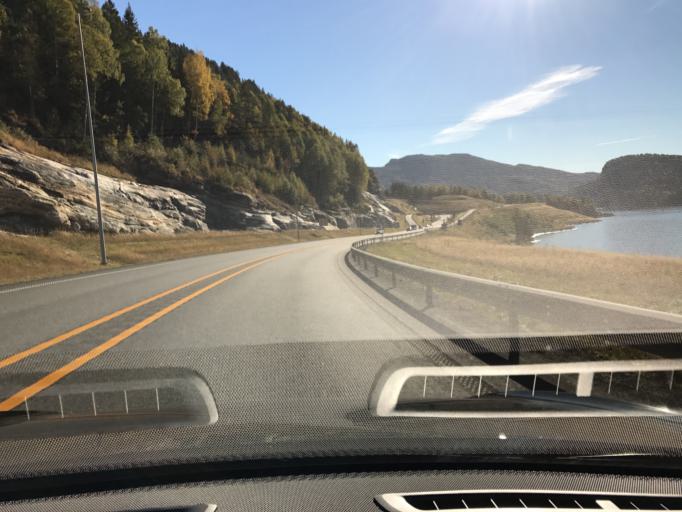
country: NO
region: Buskerud
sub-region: Krodsherad
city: Noresund
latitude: 60.2989
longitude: 9.6817
